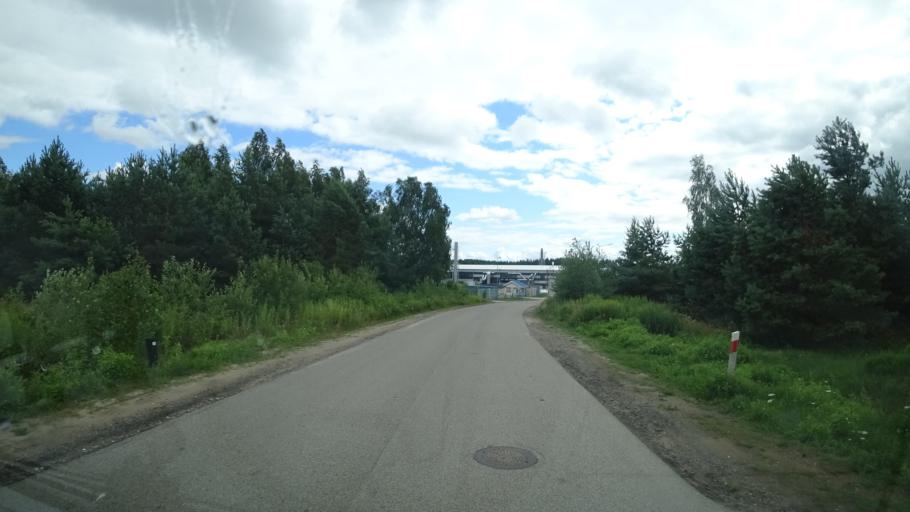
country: PL
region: Warmian-Masurian Voivodeship
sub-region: Powiat goldapski
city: Goldap
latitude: 54.3364
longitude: 22.2927
